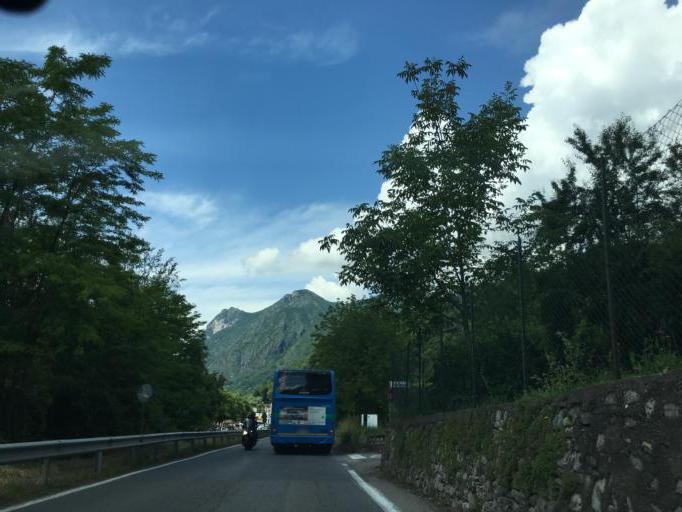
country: IT
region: Lombardy
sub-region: Provincia di Como
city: Carlazzo
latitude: 46.0429
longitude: 9.1585
